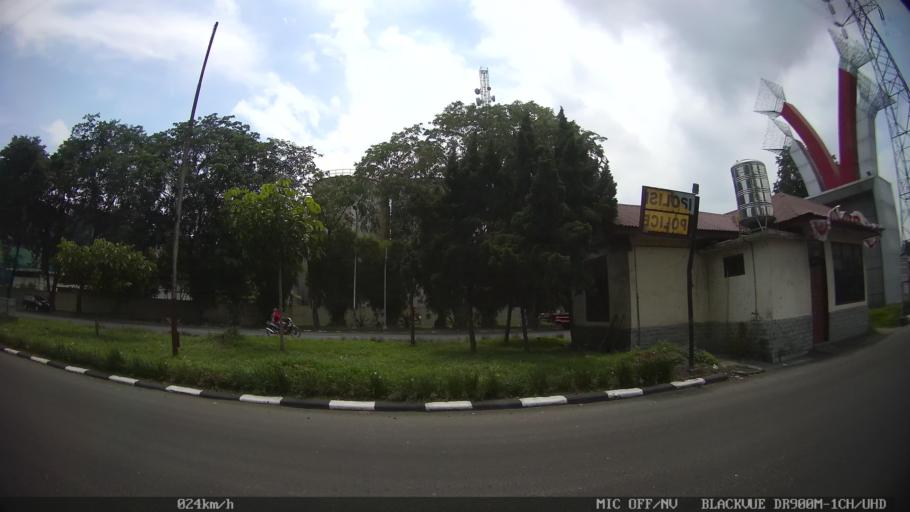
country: ID
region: North Sumatra
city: Labuhan Deli
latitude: 3.6733
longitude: 98.6832
